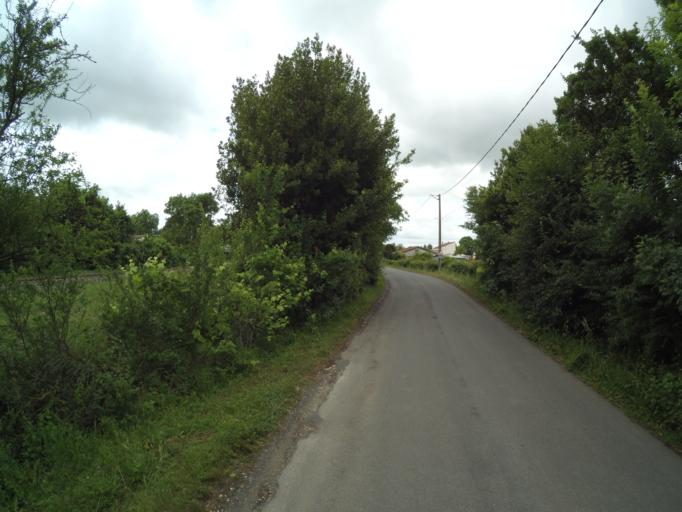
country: FR
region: Poitou-Charentes
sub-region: Departement de la Charente-Maritime
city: Breuil-Magne
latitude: 45.9702
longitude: -0.9815
